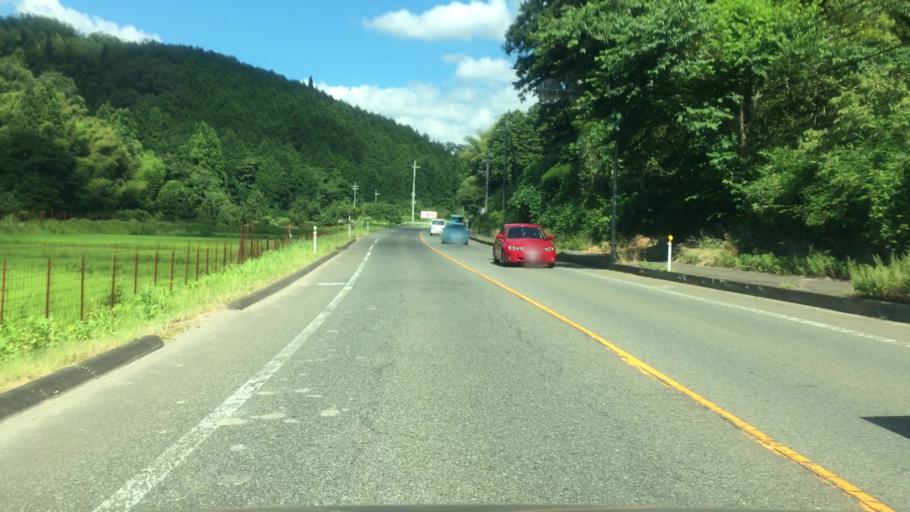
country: JP
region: Hyogo
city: Toyooka
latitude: 35.5718
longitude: 134.7784
